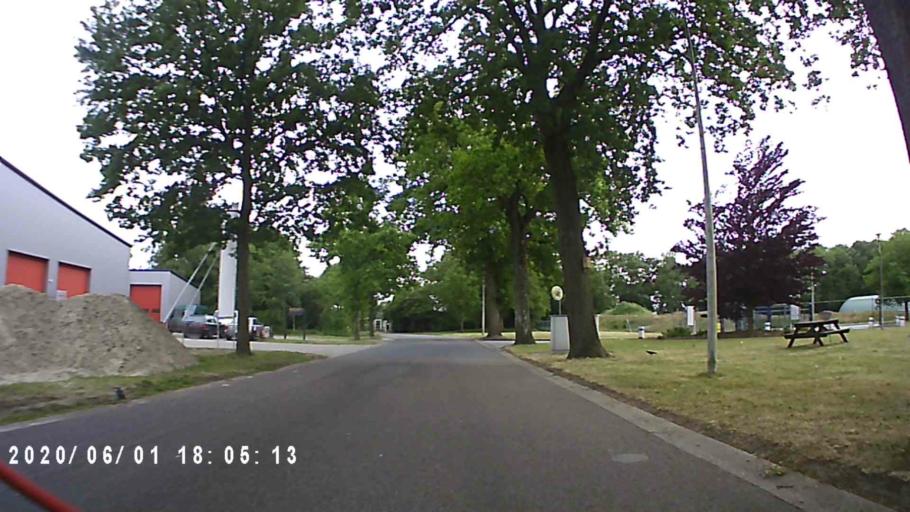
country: NL
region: Friesland
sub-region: Gemeente Tytsjerksteradiel
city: Sumar
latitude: 53.1801
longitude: 5.9941
